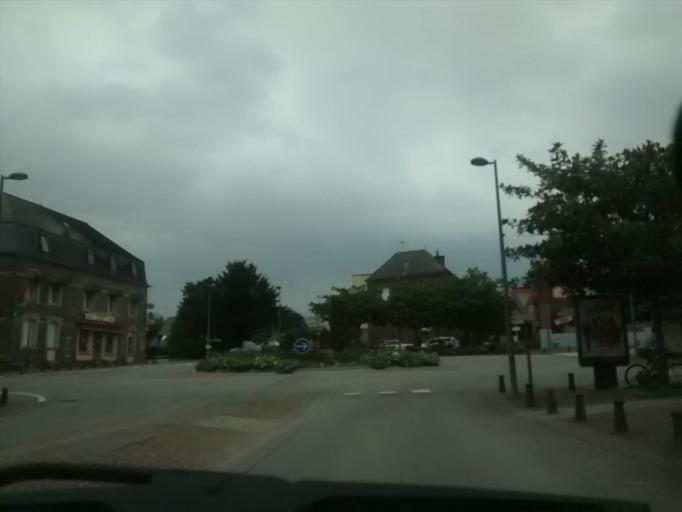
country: FR
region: Brittany
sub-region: Departement du Morbihan
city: Guer
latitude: 47.9060
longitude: -2.1238
